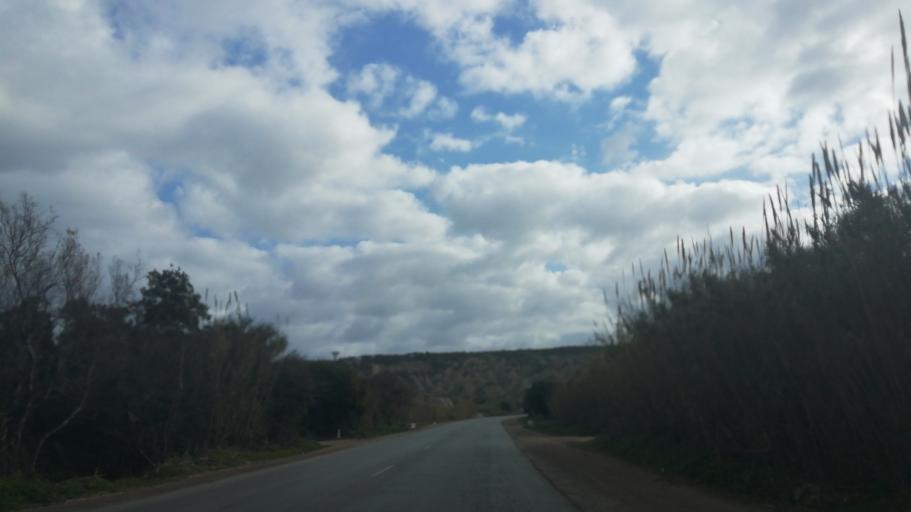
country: DZ
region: Relizane
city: Mazouna
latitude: 36.3013
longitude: 0.6635
